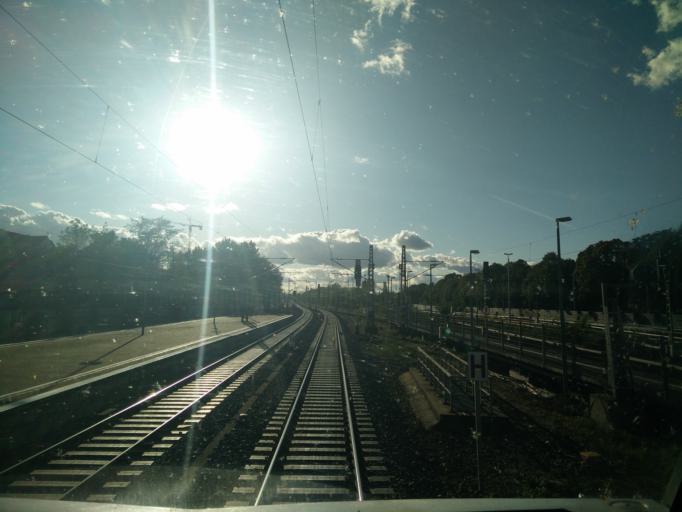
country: DE
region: Berlin
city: Halensee
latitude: 52.5040
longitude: 13.3006
